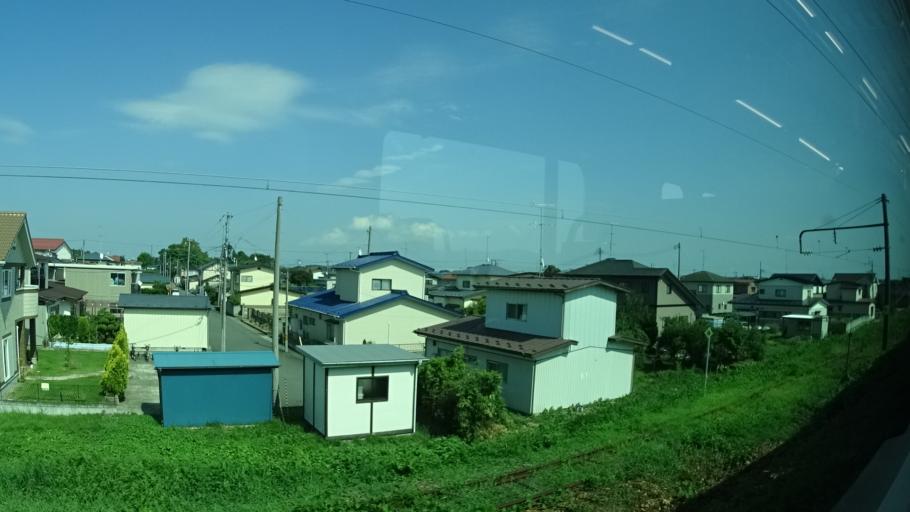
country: JP
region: Miyagi
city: Kogota
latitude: 38.5325
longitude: 141.0652
